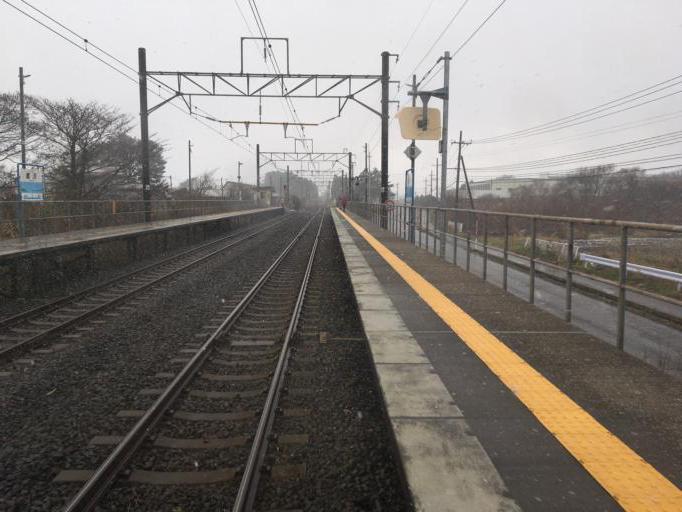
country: JP
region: Aomori
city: Aomori Shi
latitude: 40.9884
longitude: 140.6521
